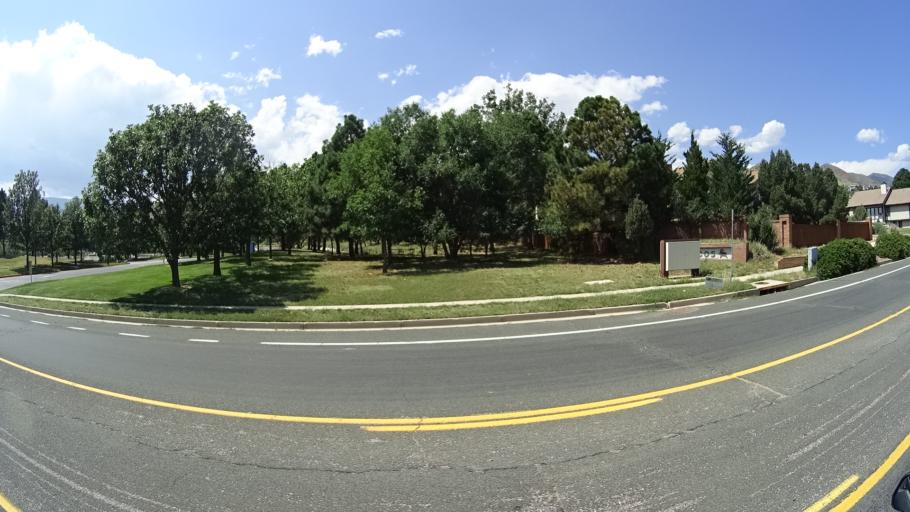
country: US
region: Colorado
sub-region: El Paso County
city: Manitou Springs
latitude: 38.9043
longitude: -104.8708
